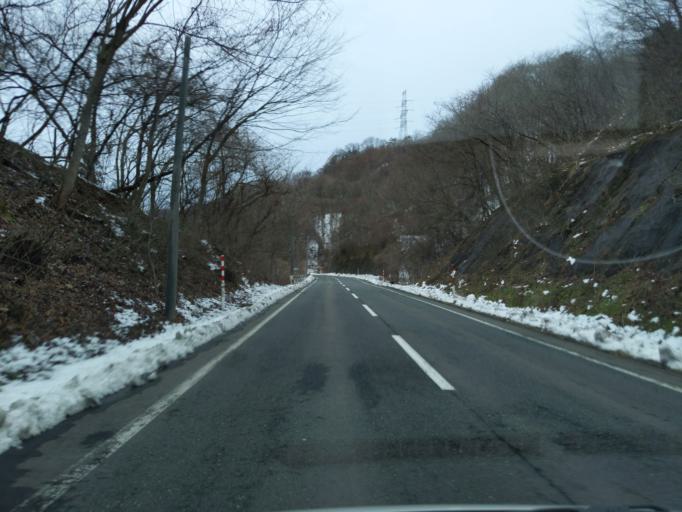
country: JP
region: Iwate
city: Mizusawa
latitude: 39.1002
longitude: 141.2658
